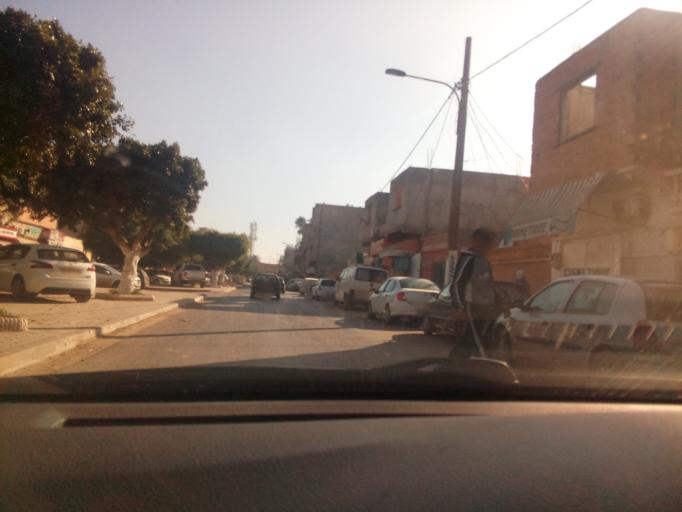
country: DZ
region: Oran
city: Es Senia
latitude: 35.6494
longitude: -0.6259
